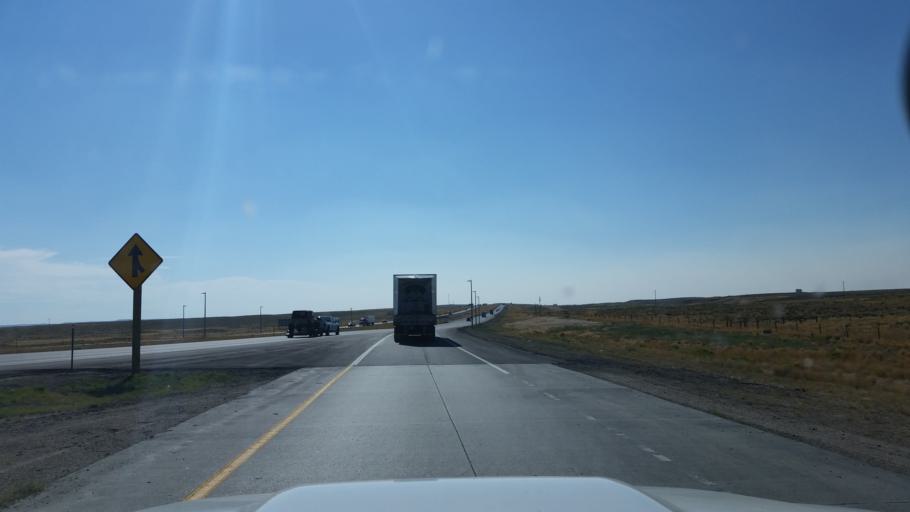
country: US
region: Wyoming
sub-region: Sweetwater County
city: Green River
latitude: 41.5426
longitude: -109.8612
